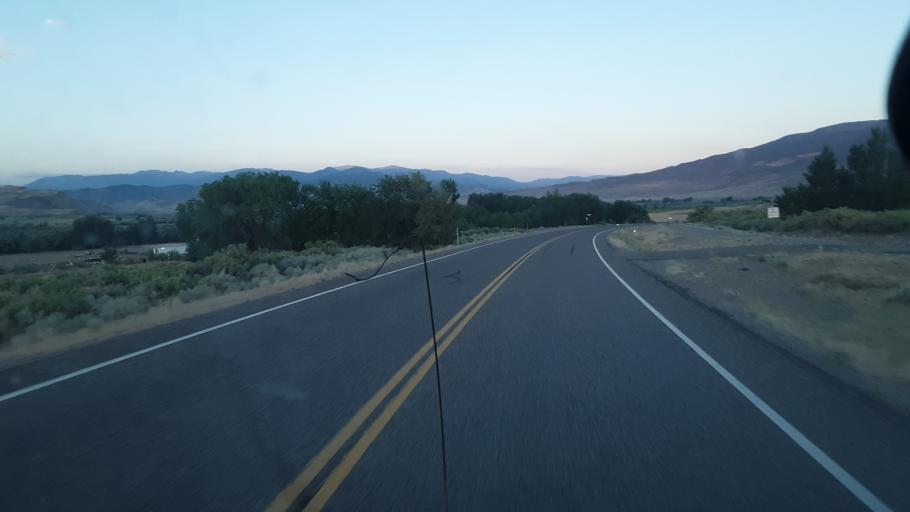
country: US
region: Utah
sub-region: Sevier County
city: Monroe
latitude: 38.6592
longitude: -112.1788
